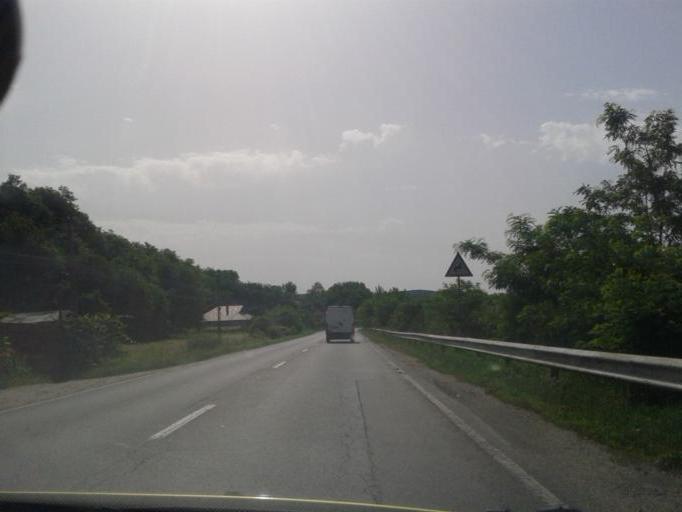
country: RO
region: Valcea
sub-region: Comuna Mihaesti
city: Mihaesti
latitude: 45.0677
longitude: 24.2283
